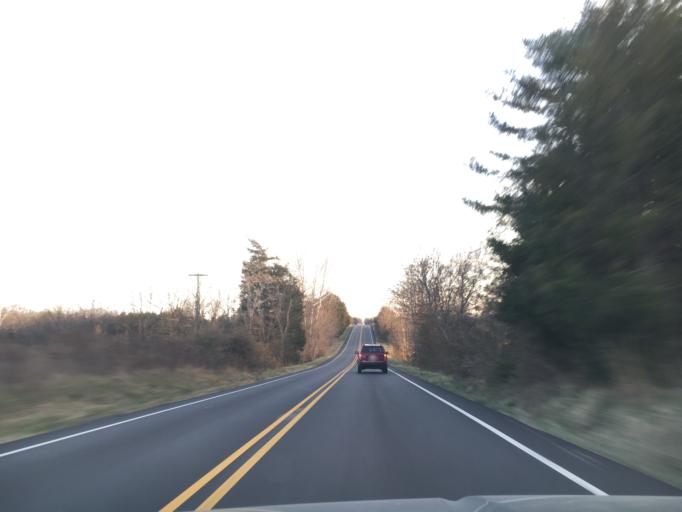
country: US
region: Virginia
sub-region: Orange County
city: Orange
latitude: 38.2266
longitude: -77.9485
